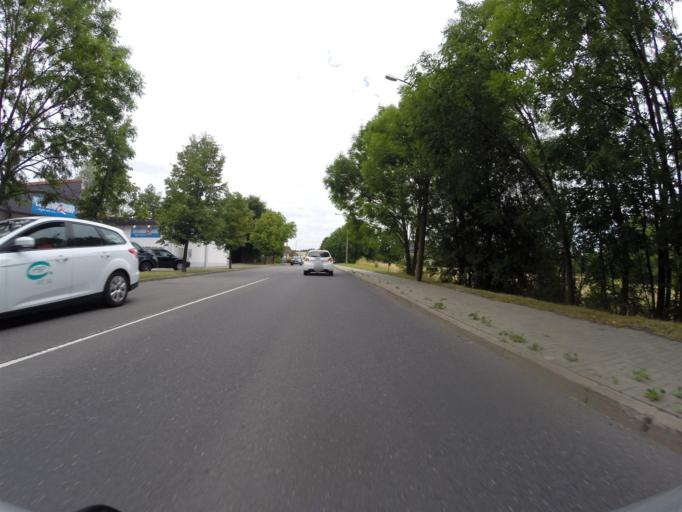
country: DE
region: Thuringia
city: Greussen
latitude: 51.2248
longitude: 10.9464
